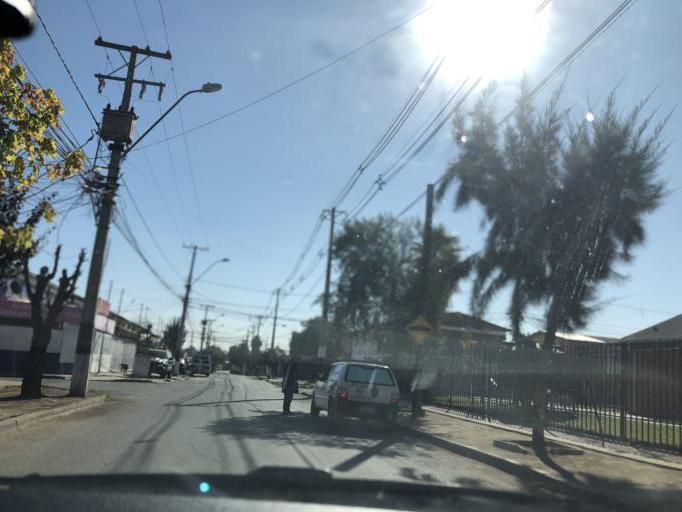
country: CL
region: Santiago Metropolitan
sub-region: Provincia de Cordillera
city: Puente Alto
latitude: -33.6196
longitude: -70.6109
